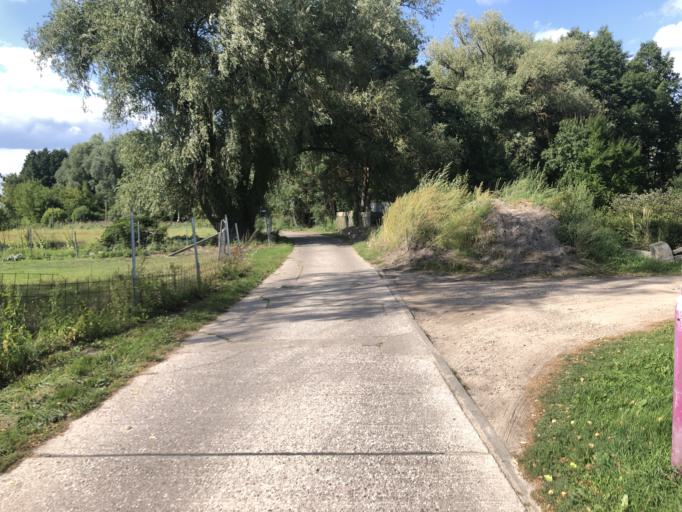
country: DE
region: Brandenburg
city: Mullrose
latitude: 52.2497
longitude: 14.4104
